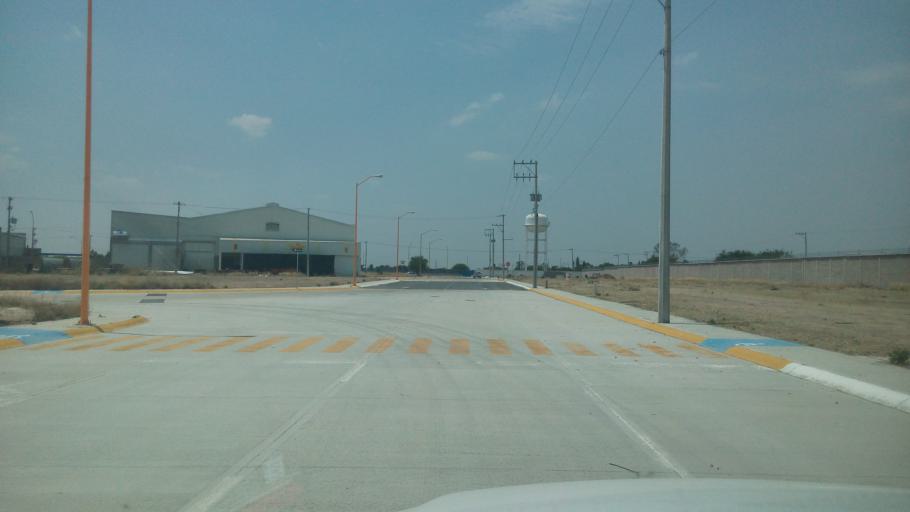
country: MX
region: Aguascalientes
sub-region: Aguascalientes
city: Villa Licenciado Jesus Teran (Calvillito)
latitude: 21.8689
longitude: -102.1782
